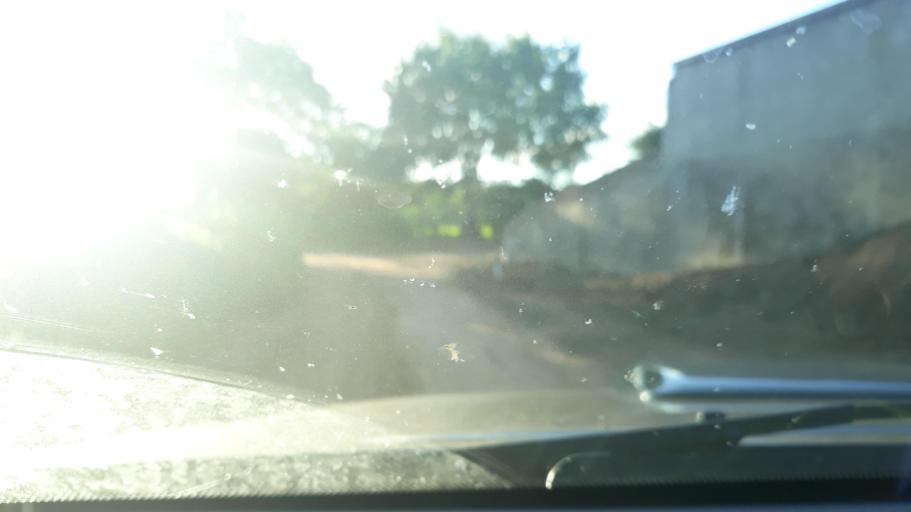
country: BR
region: Bahia
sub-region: Riacho De Santana
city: Riacho de Santana
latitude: -13.8458
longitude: -42.7594
